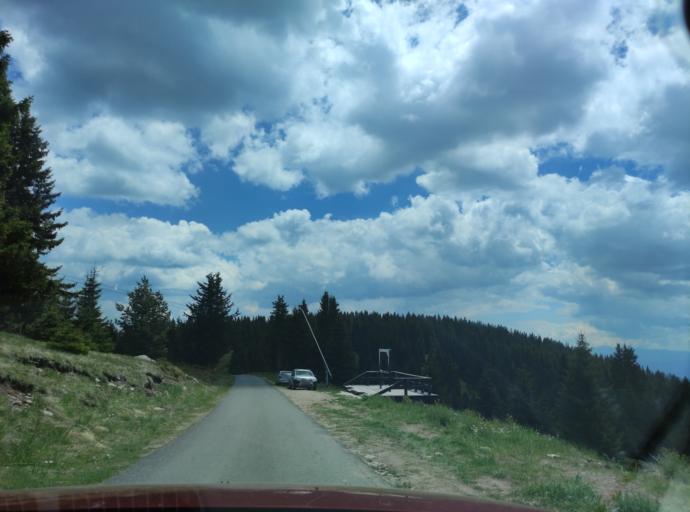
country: BG
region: Smolyan
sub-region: Obshtina Smolyan
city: Smolyan
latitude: 41.6355
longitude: 24.6782
